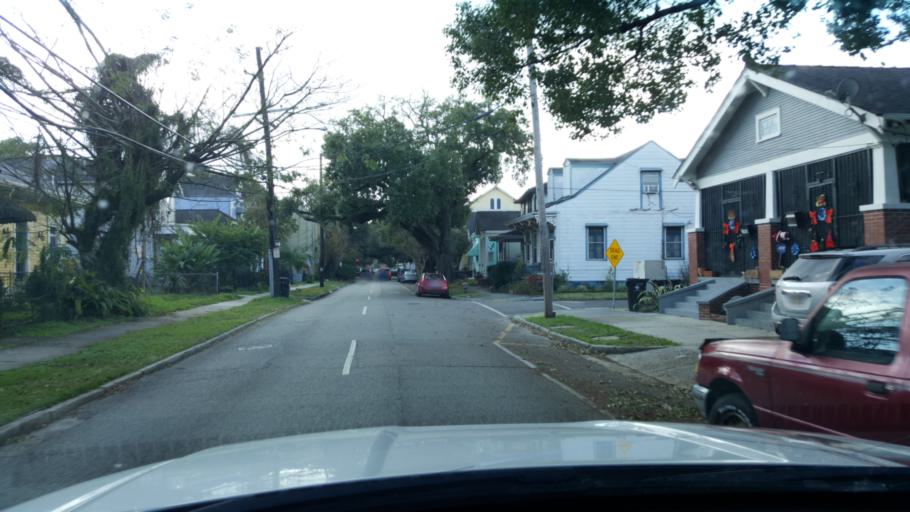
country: US
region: Louisiana
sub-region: Orleans Parish
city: New Orleans
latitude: 29.9741
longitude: -90.0729
